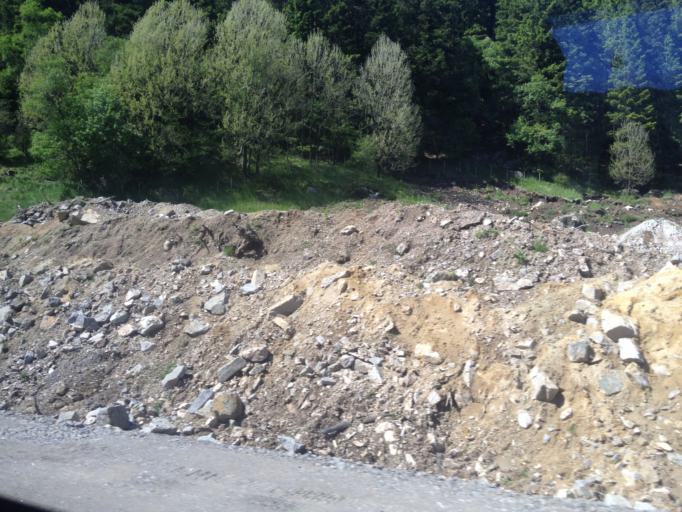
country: NO
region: Rogaland
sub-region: Bjerkreim
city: Vikesa
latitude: 58.5250
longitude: 6.1212
